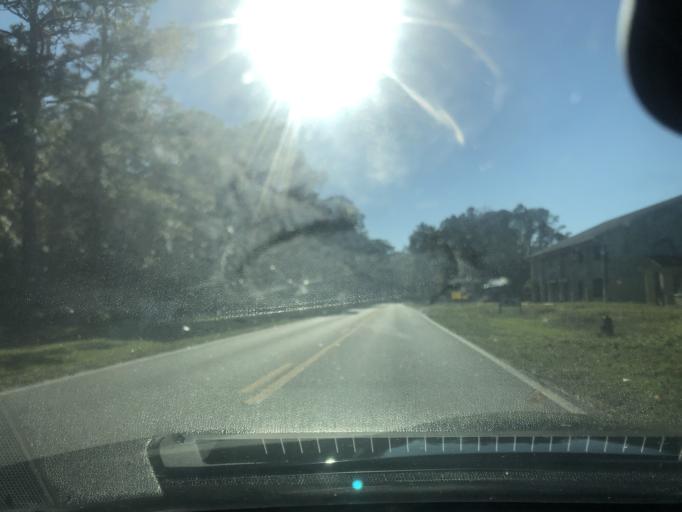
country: US
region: Florida
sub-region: Citrus County
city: Homosassa Springs
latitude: 28.8087
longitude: -82.5707
